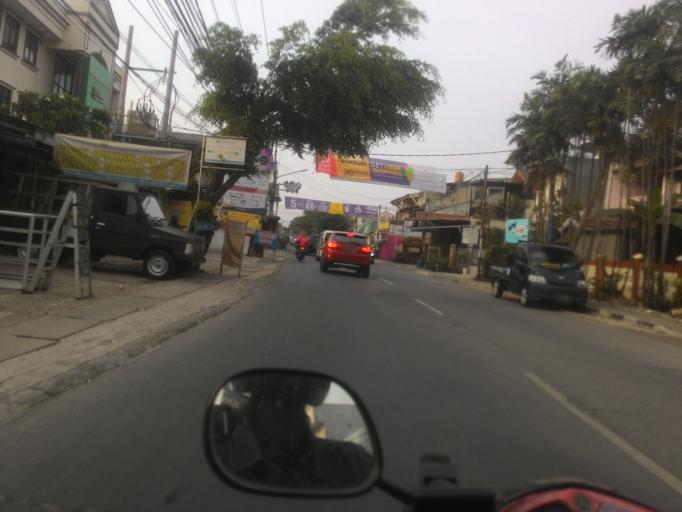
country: ID
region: West Java
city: Depok
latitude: -6.4003
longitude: 106.8363
